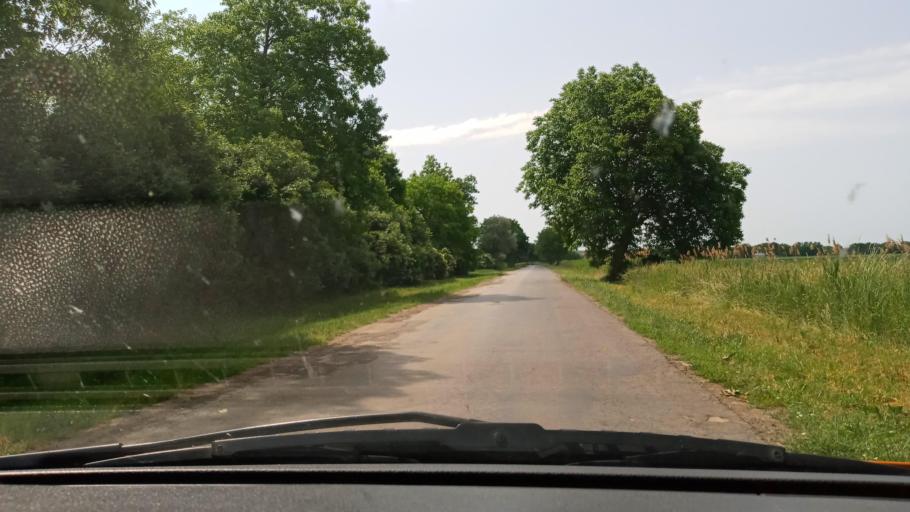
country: HU
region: Baranya
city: Szentlorinc
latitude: 45.9986
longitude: 18.0370
